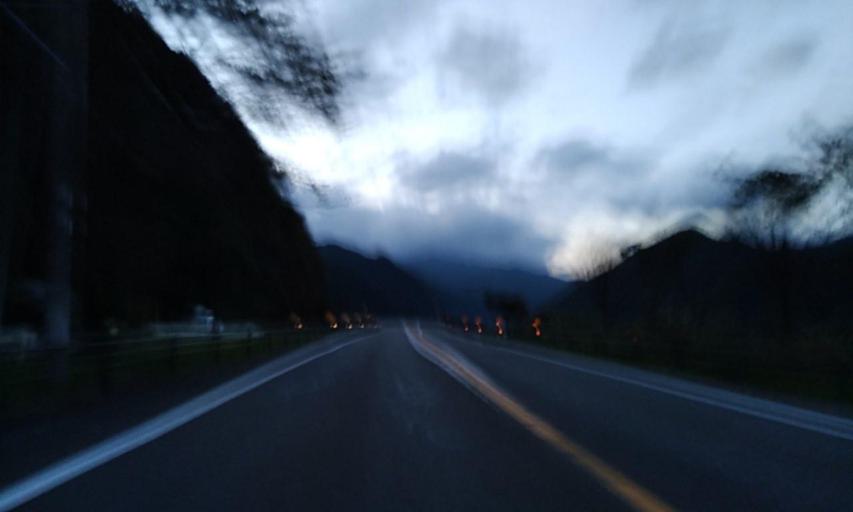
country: JP
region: Wakayama
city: Shingu
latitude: 33.7242
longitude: 135.9616
